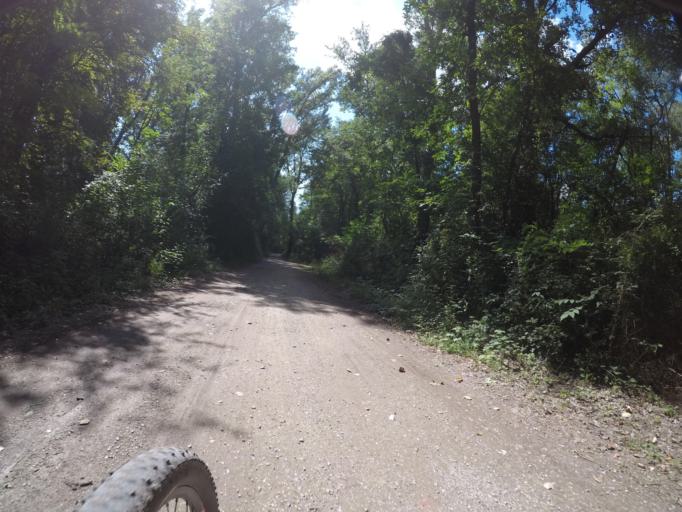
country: AT
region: Lower Austria
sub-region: Politischer Bezirk Ganserndorf
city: Gross-Enzersdorf
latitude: 48.1777
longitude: 16.5322
